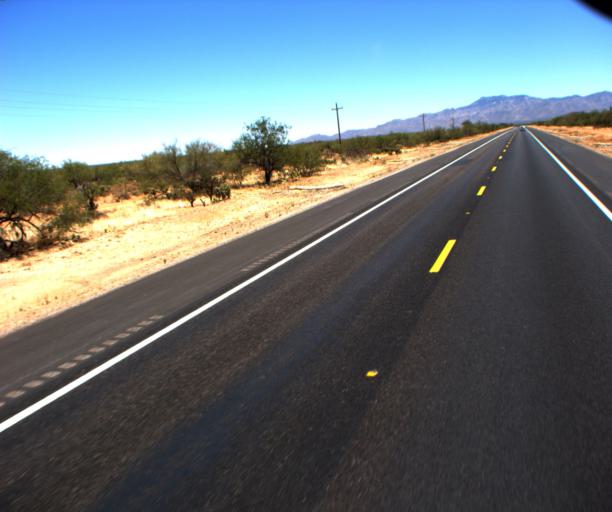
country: US
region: Arizona
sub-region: Pima County
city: Sells
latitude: 31.9176
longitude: -111.8442
